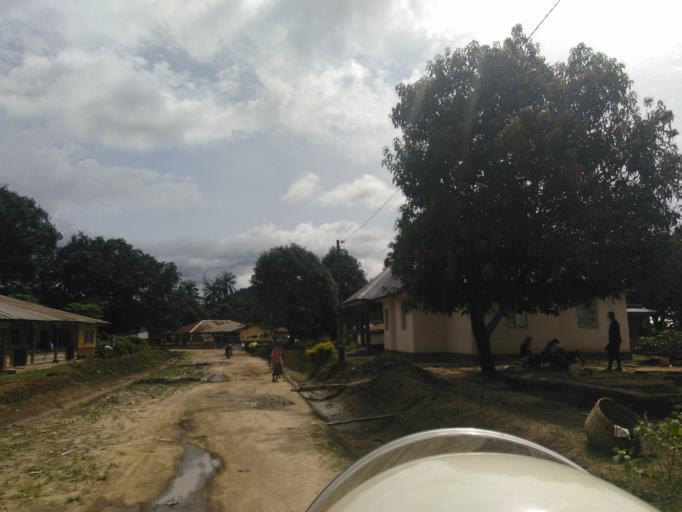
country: SL
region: Northern Province
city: Makali
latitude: 8.6282
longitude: -11.6625
